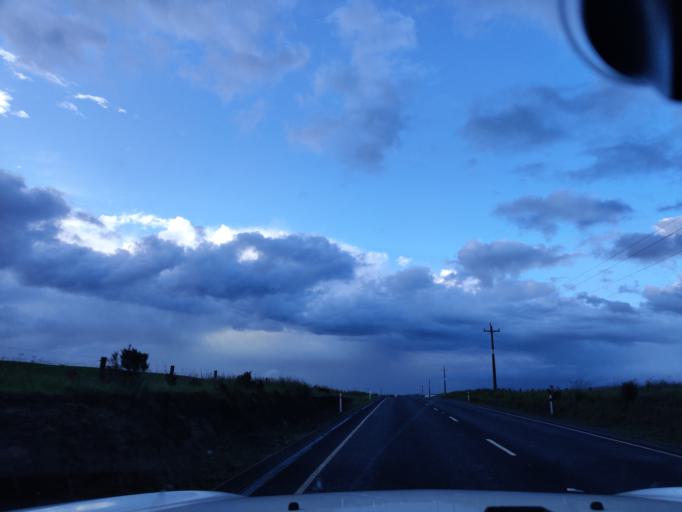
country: NZ
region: Waikato
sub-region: South Waikato District
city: Tokoroa
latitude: -38.3880
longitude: 175.7810
